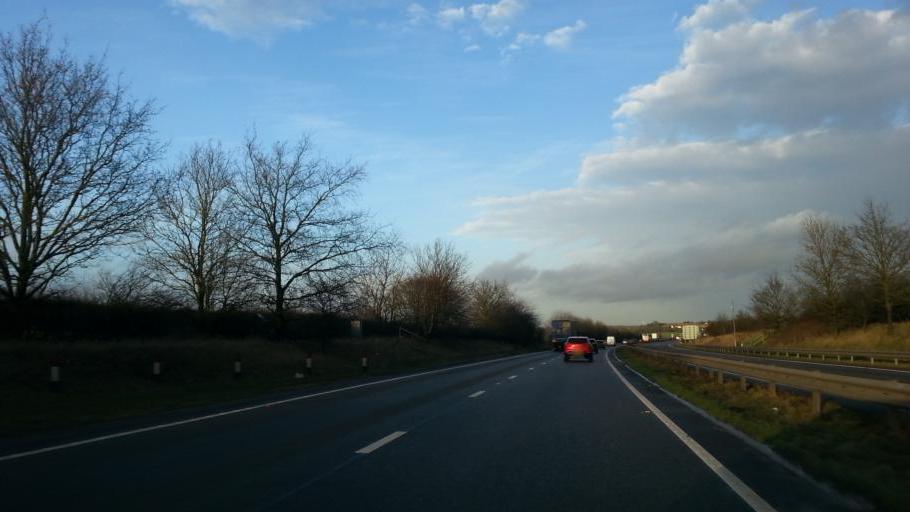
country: GB
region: England
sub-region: Leicestershire
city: Donisthorpe
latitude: 52.6986
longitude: -1.5442
